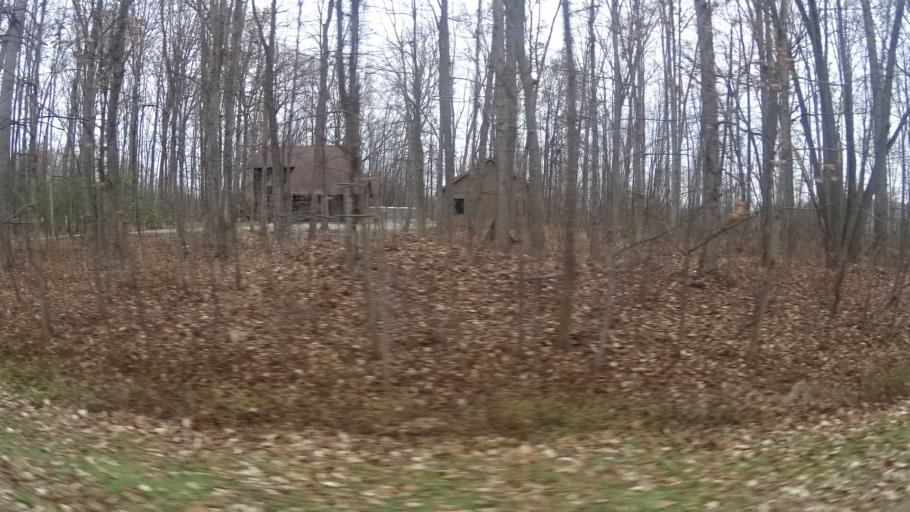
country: US
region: Ohio
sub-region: Lorain County
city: Eaton Estates
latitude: 41.2922
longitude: -81.9596
